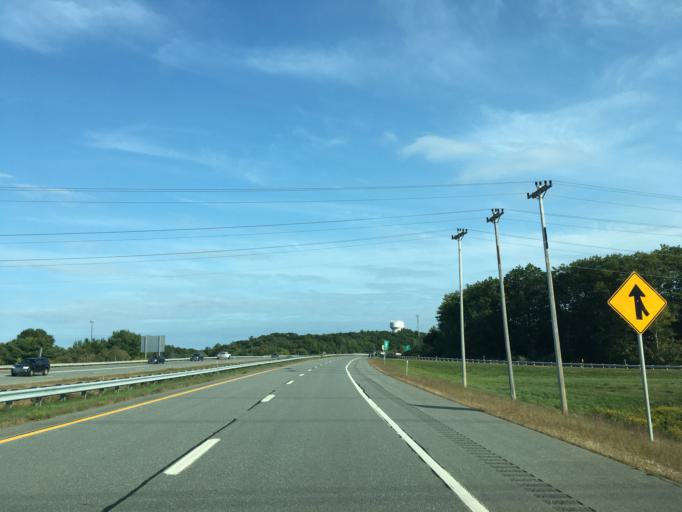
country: US
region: New Hampshire
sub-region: Rockingham County
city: Hampton
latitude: 42.9609
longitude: -70.8603
